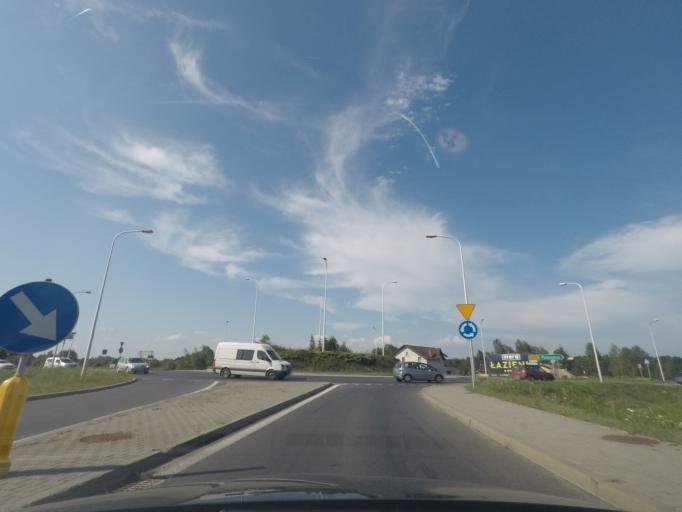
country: PL
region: Silesian Voivodeship
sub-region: Zory
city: Zory
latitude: 50.0582
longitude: 18.6826
